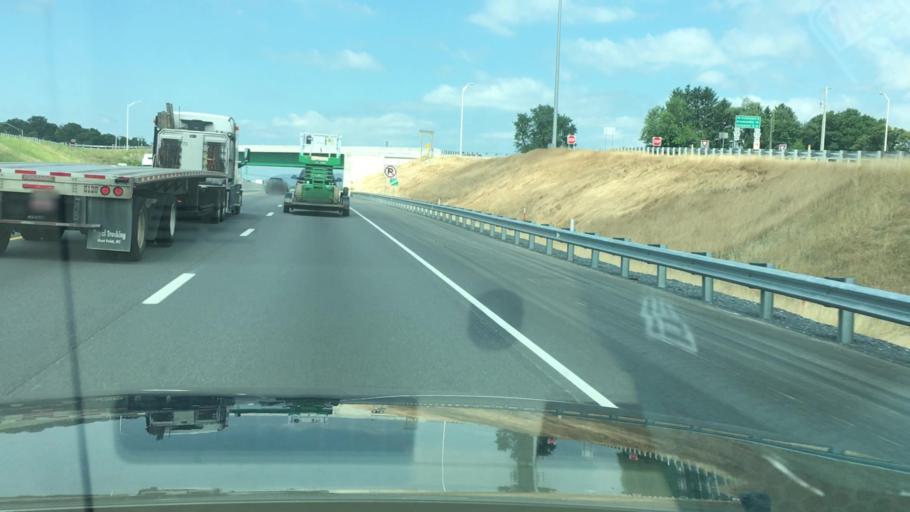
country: US
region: Pennsylvania
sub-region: Berks County
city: Kutztown
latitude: 40.5774
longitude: -75.7965
